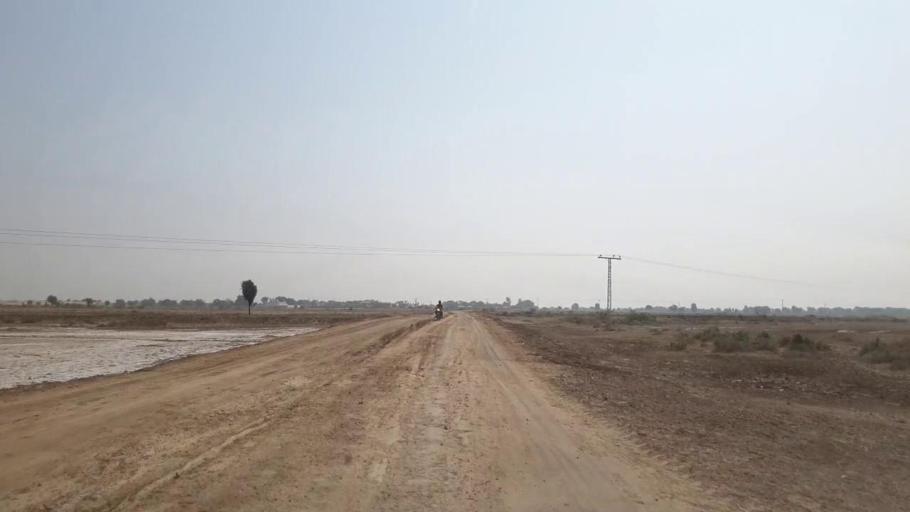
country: PK
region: Sindh
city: Mirpur Khas
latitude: 25.6430
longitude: 69.1432
